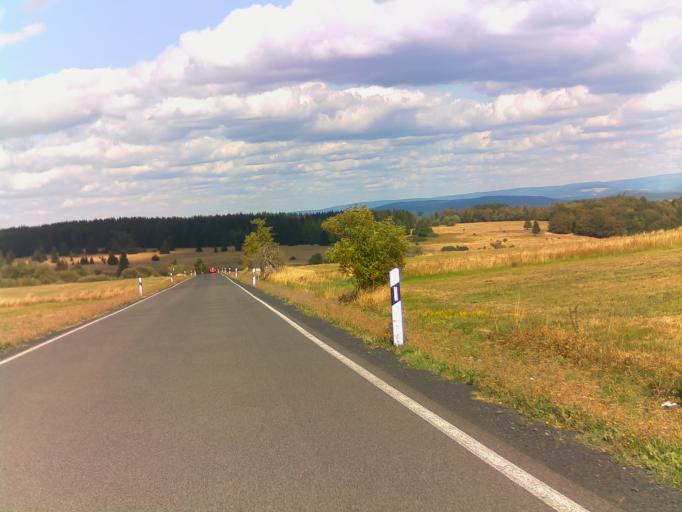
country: DE
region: Thuringia
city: Birx
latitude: 50.5000
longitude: 10.0679
